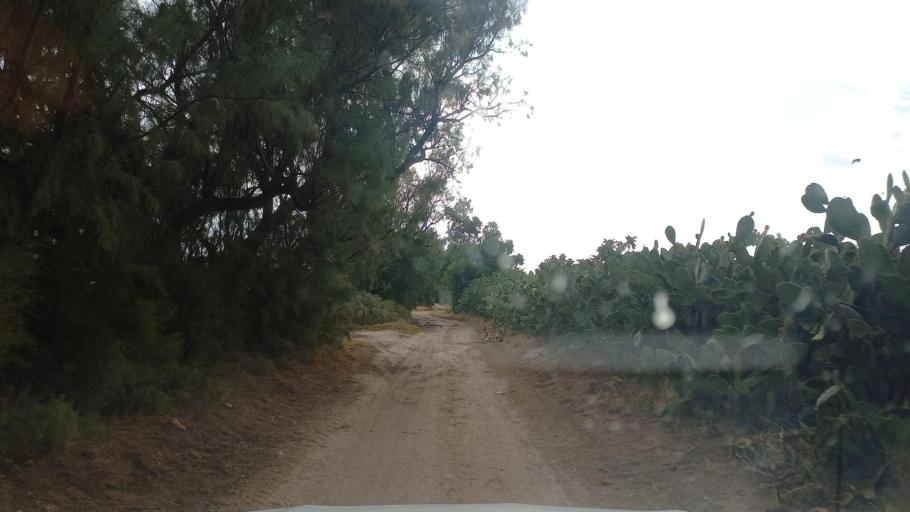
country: TN
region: Al Qasrayn
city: Sbiba
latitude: 35.2940
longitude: 9.0619
